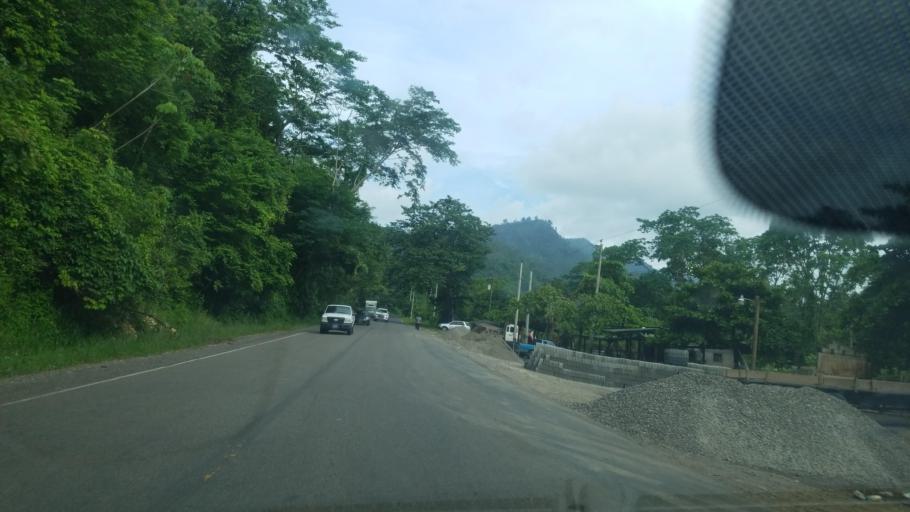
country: HN
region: Santa Barbara
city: Petoa
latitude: 15.2468
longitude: -88.2715
